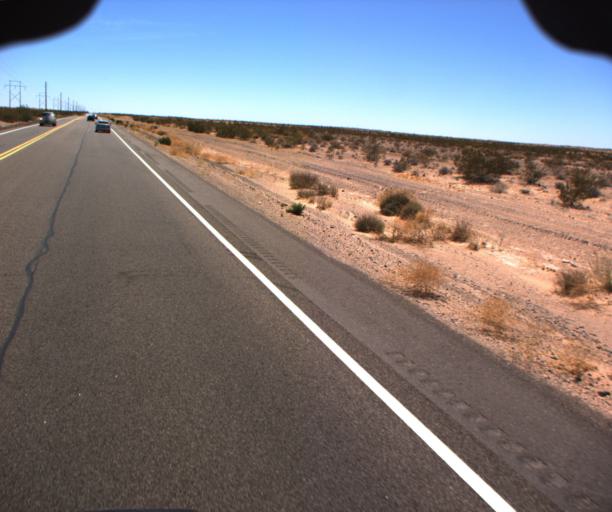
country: US
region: Arizona
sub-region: La Paz County
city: Parker
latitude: 33.9755
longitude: -114.2169
